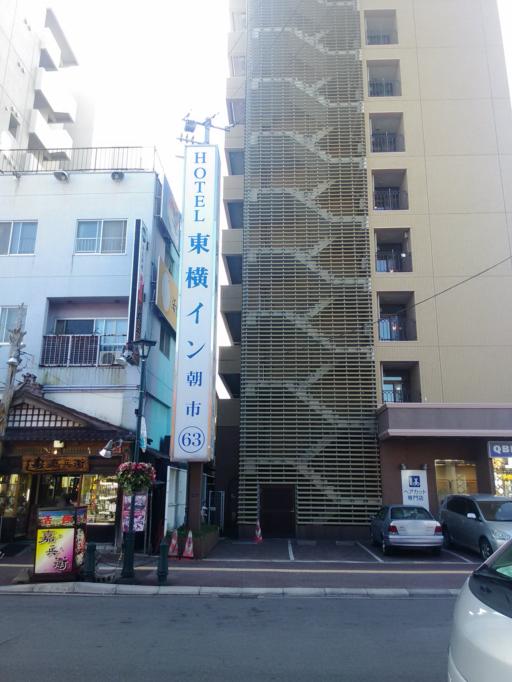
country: JP
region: Hokkaido
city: Hakodate
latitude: 41.7708
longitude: 140.7239
